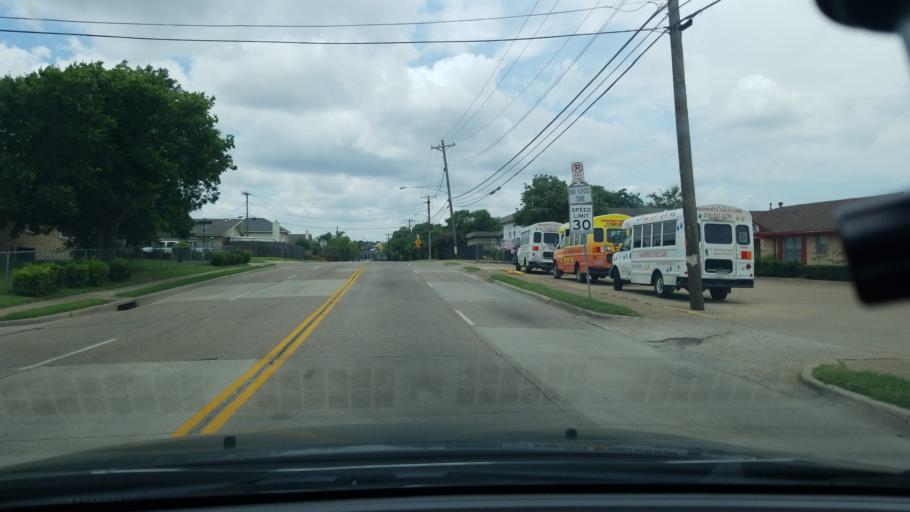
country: US
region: Texas
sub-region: Dallas County
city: Mesquite
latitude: 32.8147
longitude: -96.6844
